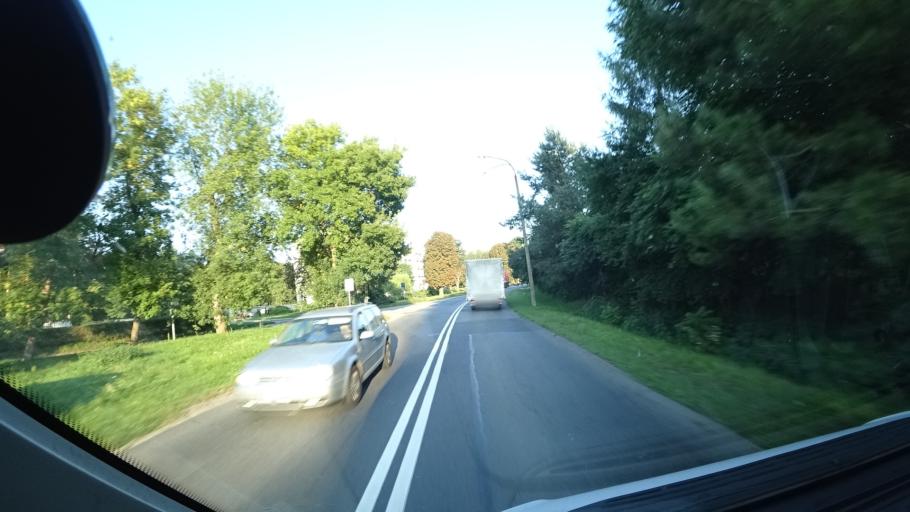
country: PL
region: Silesian Voivodeship
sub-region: Powiat gliwicki
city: Rudziniec
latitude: 50.2778
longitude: 18.3676
